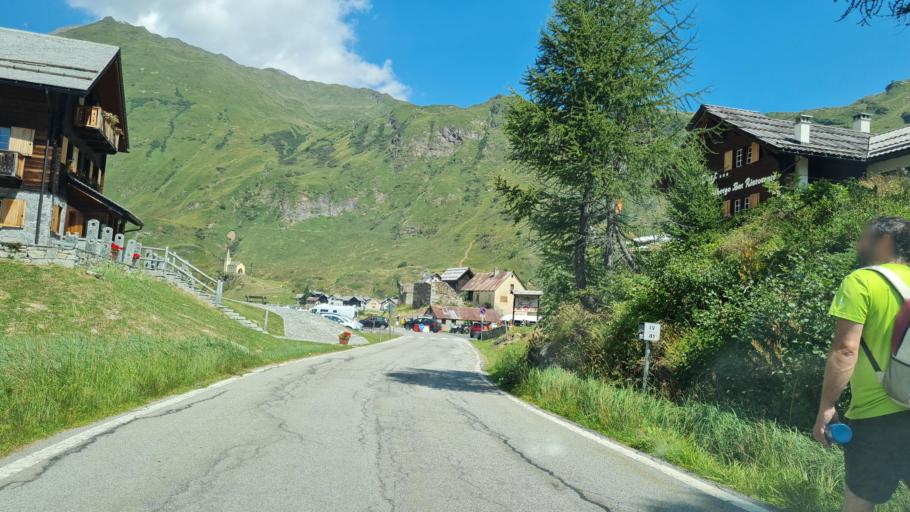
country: IT
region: Piedmont
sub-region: Provincia Verbano-Cusio-Ossola
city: Formazza
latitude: 46.4191
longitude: 8.4165
